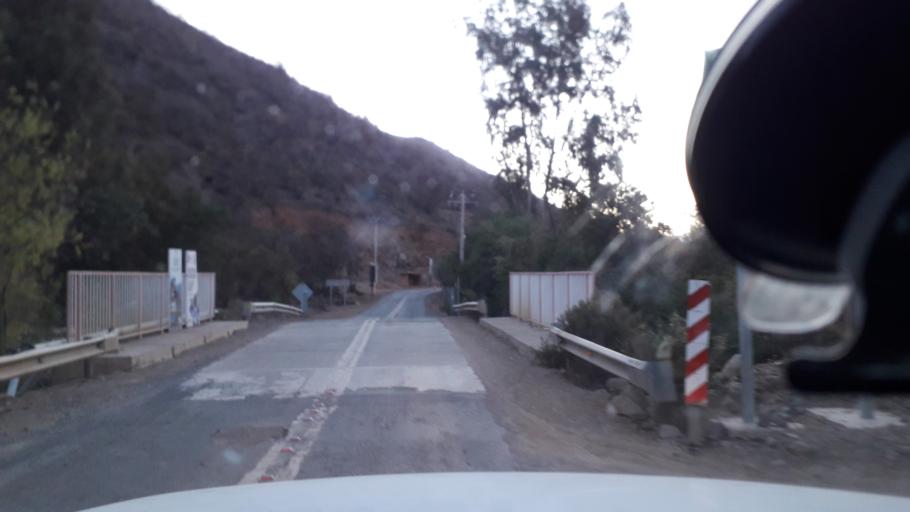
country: CL
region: Valparaiso
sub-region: Provincia de Marga Marga
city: Limache
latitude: -33.1816
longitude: -71.1115
